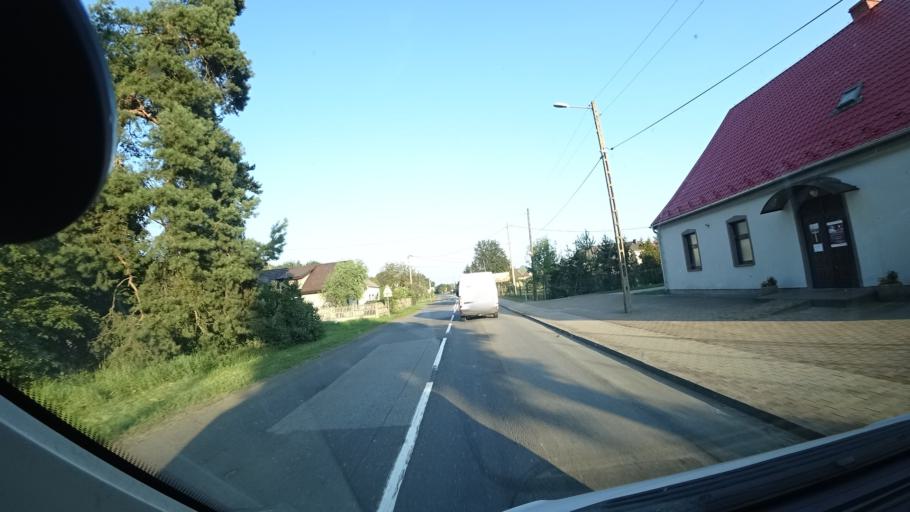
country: PL
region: Opole Voivodeship
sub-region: Powiat kedzierzynsko-kozielski
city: Dziergowice
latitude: 50.2821
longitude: 18.3203
